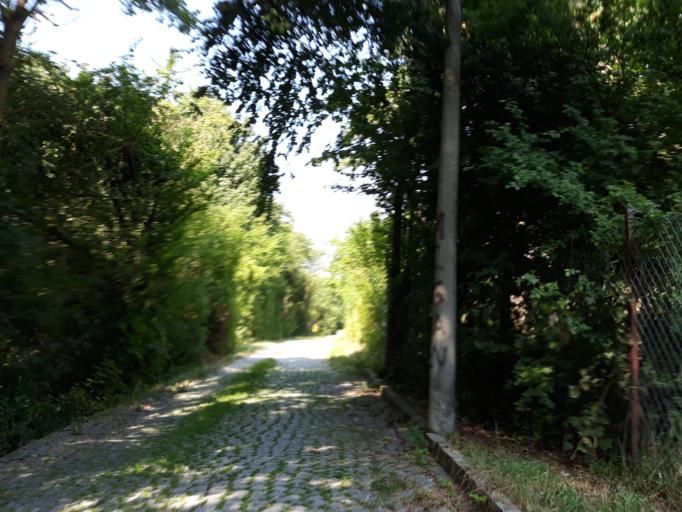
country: DE
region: Baden-Wuerttemberg
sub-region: Regierungsbezirk Stuttgart
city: Sindelfingen
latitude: 48.7010
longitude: 9.0138
